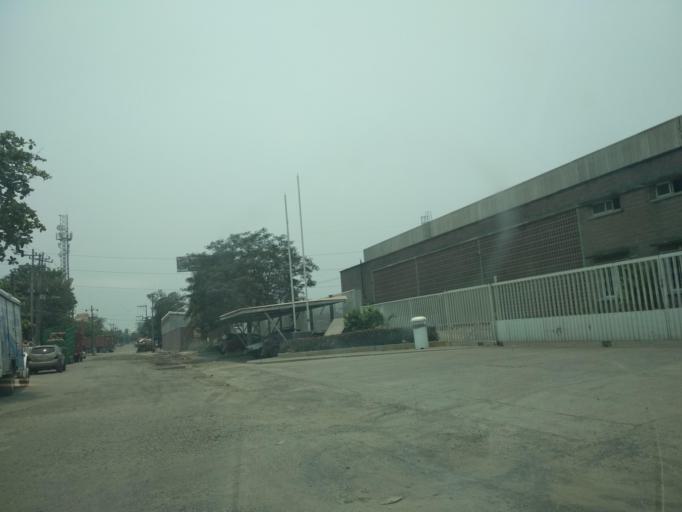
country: MX
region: Veracruz
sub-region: Veracruz
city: Lomas de Rio Medio Cuatro
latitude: 19.1701
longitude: -96.2324
